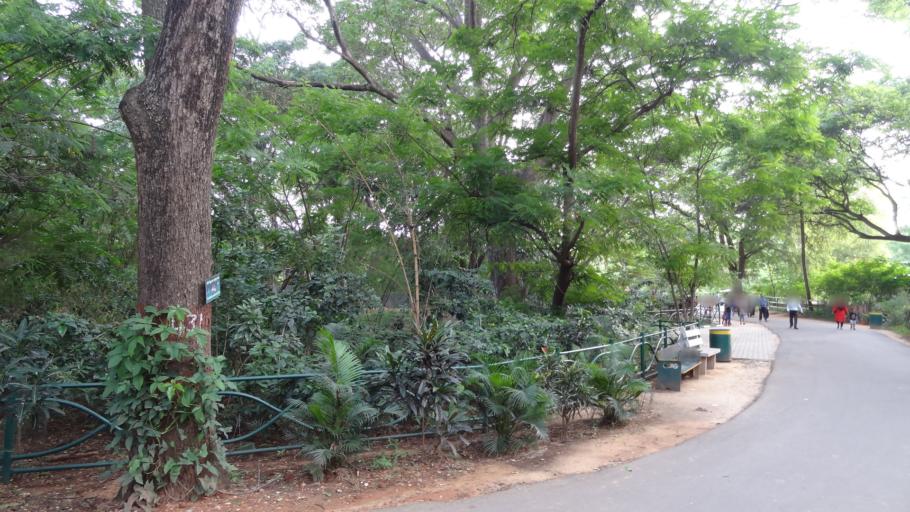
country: IN
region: Karnataka
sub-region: Mysore
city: Mysore
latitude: 12.3016
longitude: 76.6704
